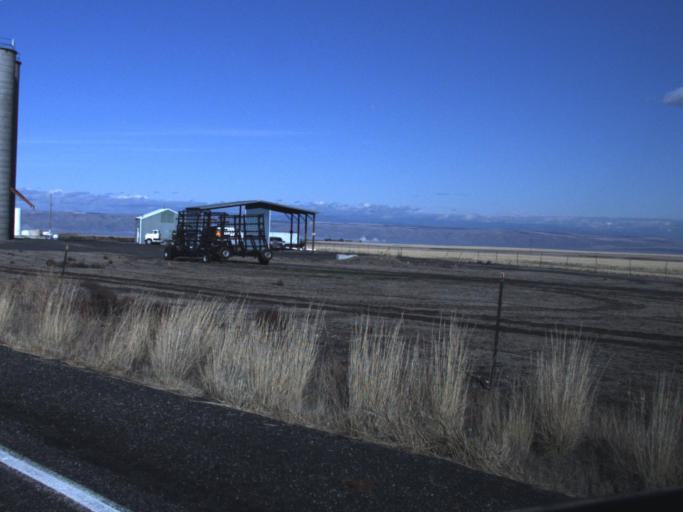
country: US
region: Washington
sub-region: Asotin County
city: Asotin
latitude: 46.2039
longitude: -117.0699
